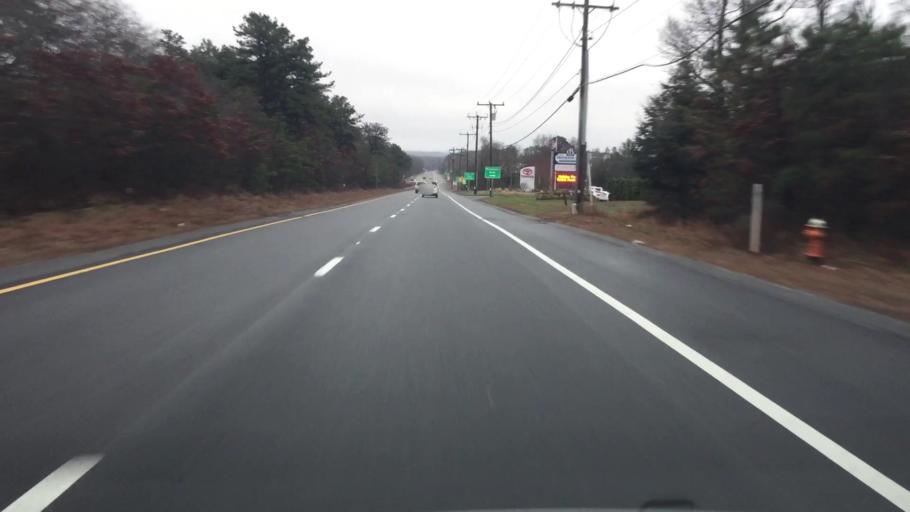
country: US
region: Massachusetts
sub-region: Barnstable County
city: Bourne
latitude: 41.7232
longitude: -70.5847
